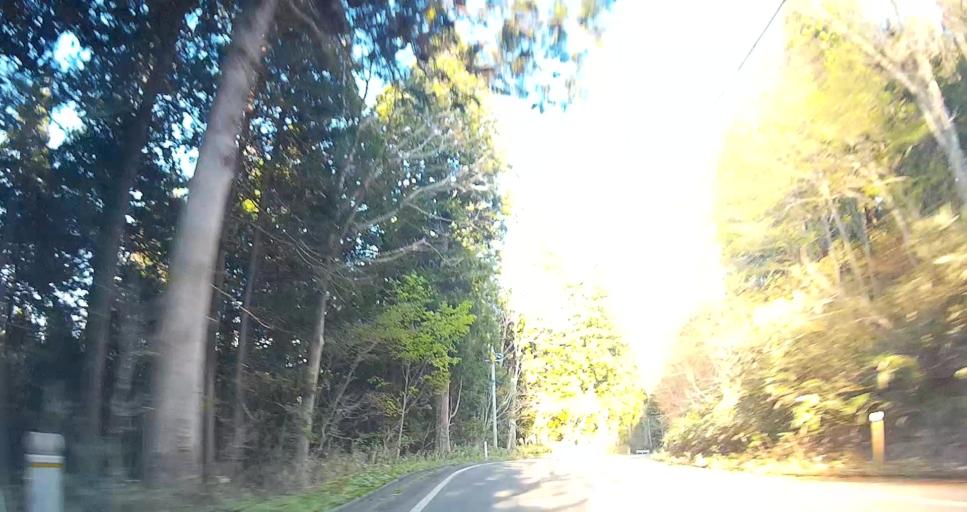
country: JP
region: Aomori
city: Mutsu
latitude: 41.3152
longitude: 141.1232
